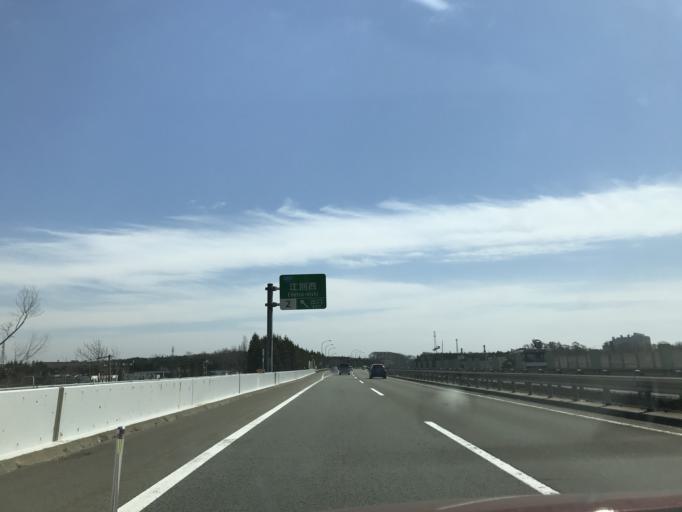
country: JP
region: Hokkaido
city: Ebetsu
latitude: 43.0944
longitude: 141.4905
